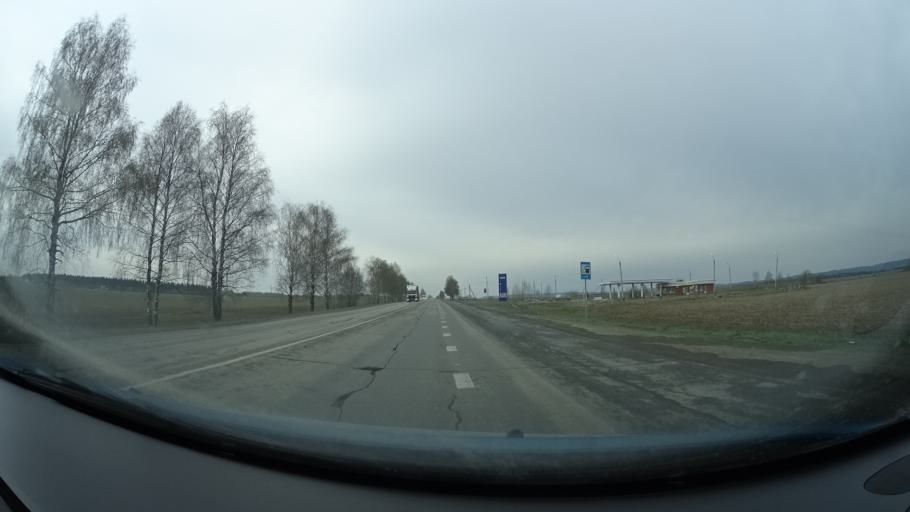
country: RU
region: Perm
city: Ust'-Kachka
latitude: 58.0712
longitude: 55.6333
